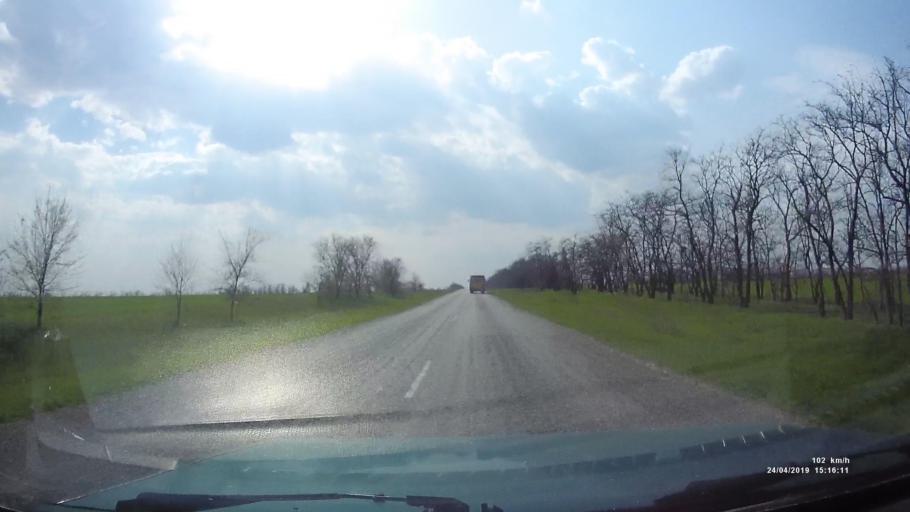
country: RU
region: Rostov
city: Remontnoye
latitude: 46.5455
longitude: 43.2192
